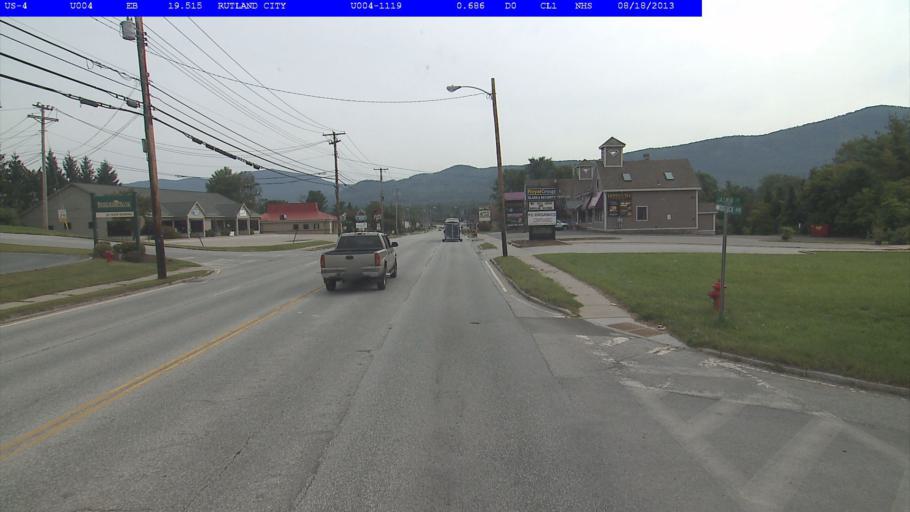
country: US
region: Vermont
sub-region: Rutland County
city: Rutland
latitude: 43.6157
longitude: -72.9611
